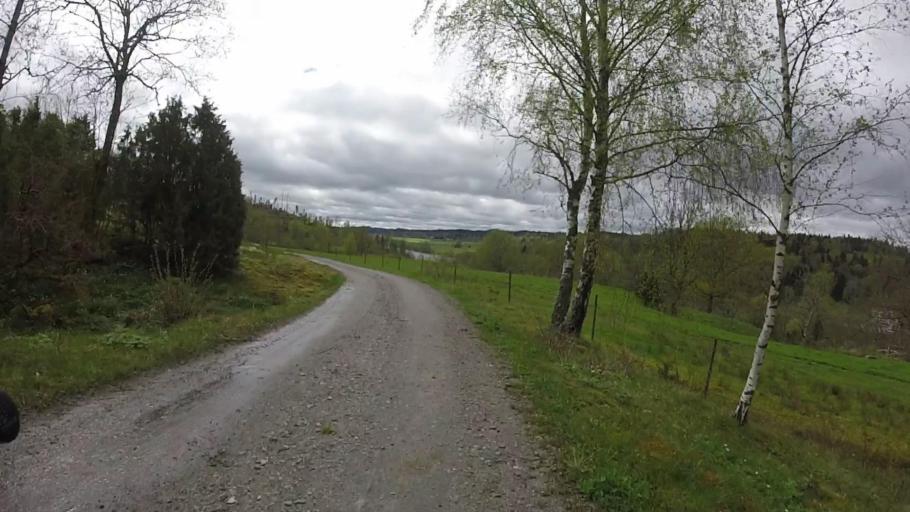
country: SE
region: Vaestra Goetaland
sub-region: Trollhattan
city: Sjuntorp
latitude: 58.2426
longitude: 12.2076
